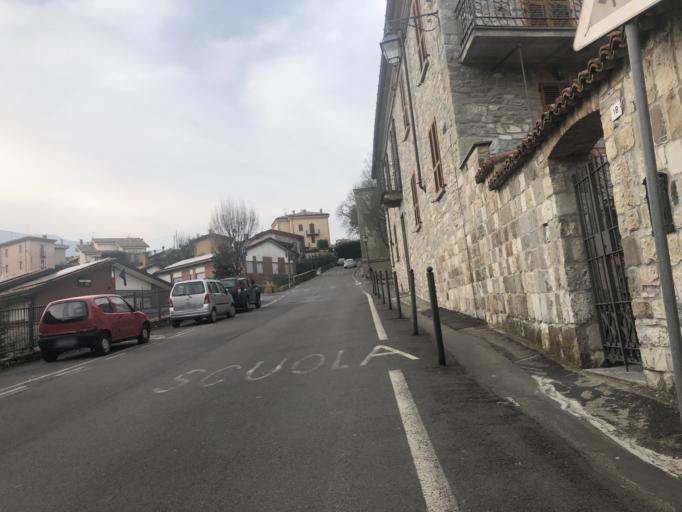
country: IT
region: Emilia-Romagna
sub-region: Provincia di Piacenza
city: Bobbio
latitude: 44.7669
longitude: 9.3833
